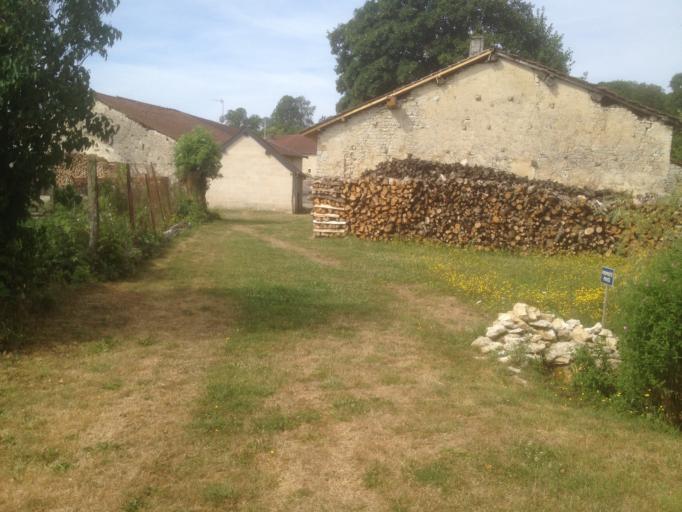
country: FR
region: Champagne-Ardenne
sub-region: Departement de la Haute-Marne
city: Joinville
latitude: 48.4719
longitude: 5.2882
